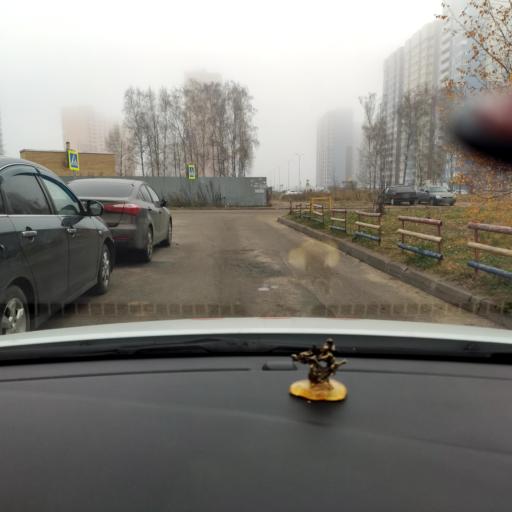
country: RU
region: Tatarstan
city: Osinovo
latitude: 55.8693
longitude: 48.8803
